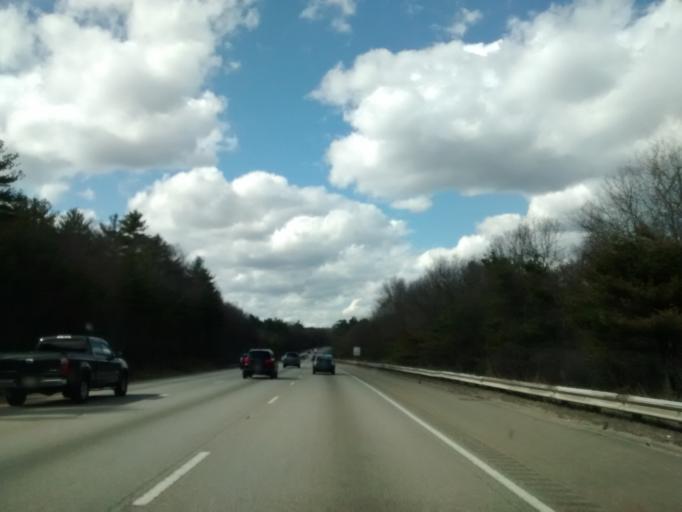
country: US
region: Massachusetts
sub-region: Middlesex County
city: Hopkinton
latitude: 42.2238
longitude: -71.5479
